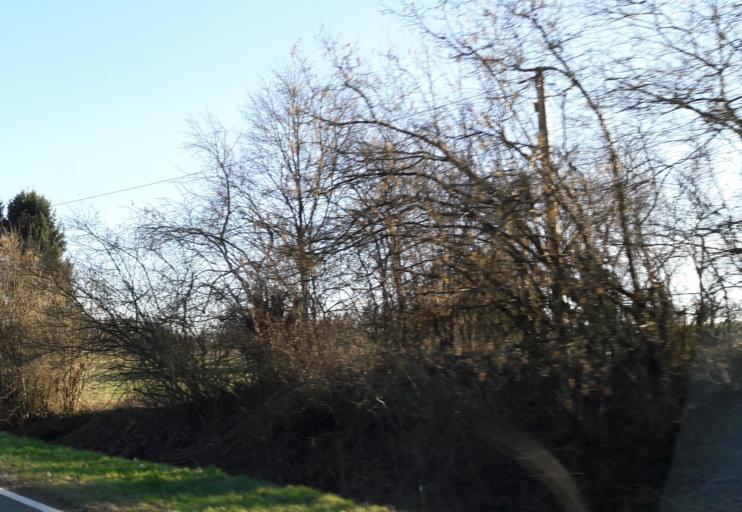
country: DE
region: Saarland
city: Illingen
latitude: 49.4059
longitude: 7.0758
